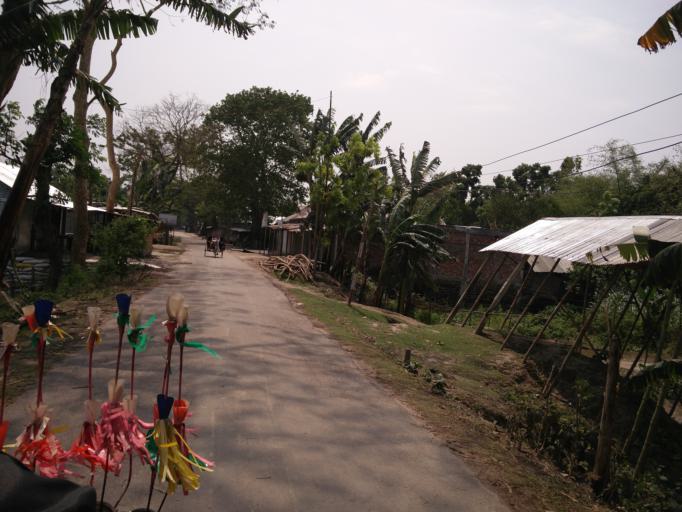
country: BD
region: Dhaka
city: Sherpur
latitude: 24.9465
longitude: 90.1605
